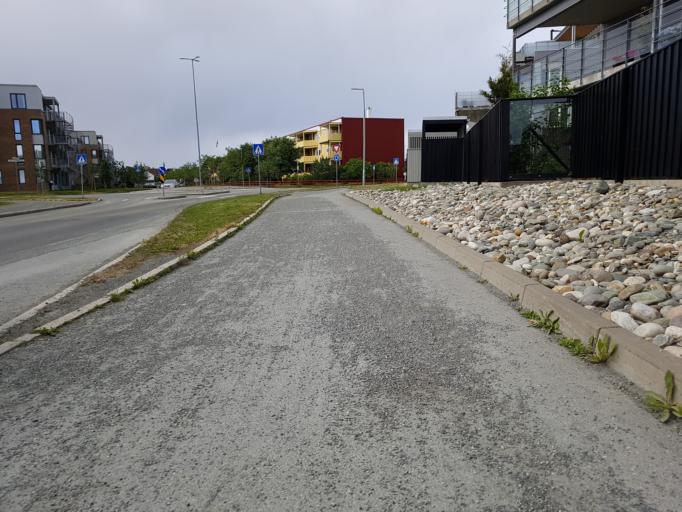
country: NO
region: Sor-Trondelag
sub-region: Trondheim
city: Trondheim
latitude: 63.4313
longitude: 10.4497
